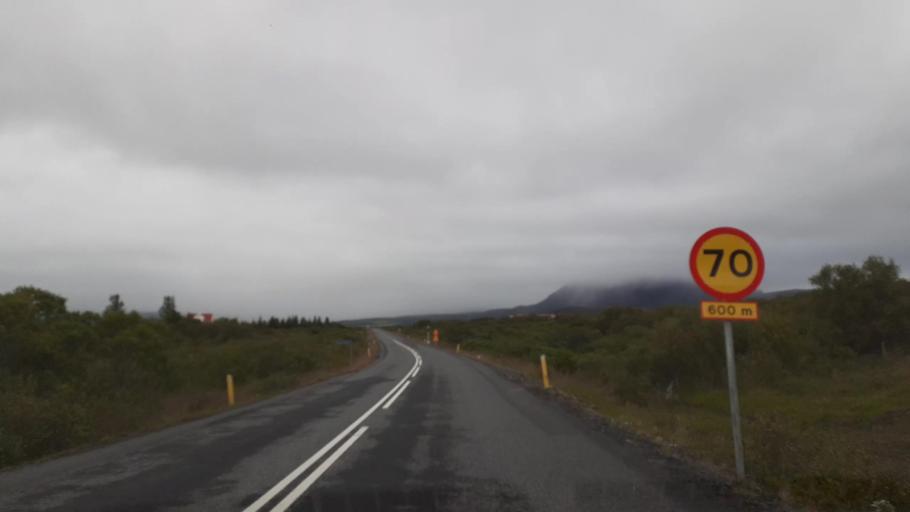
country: IS
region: Northeast
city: Husavik
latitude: 66.0715
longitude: -16.4376
